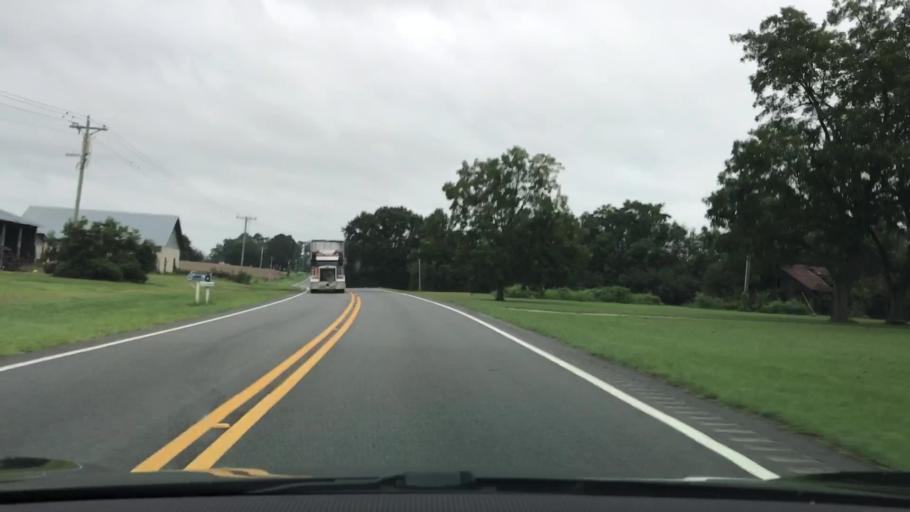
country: US
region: Alabama
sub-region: Covington County
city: Opp
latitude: 31.2735
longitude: -86.1585
